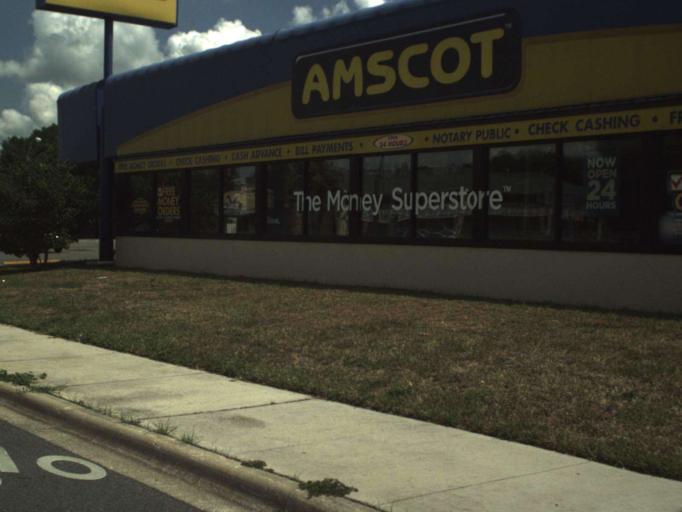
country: US
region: Florida
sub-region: Lake County
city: Leesburg
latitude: 28.8207
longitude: -81.8819
